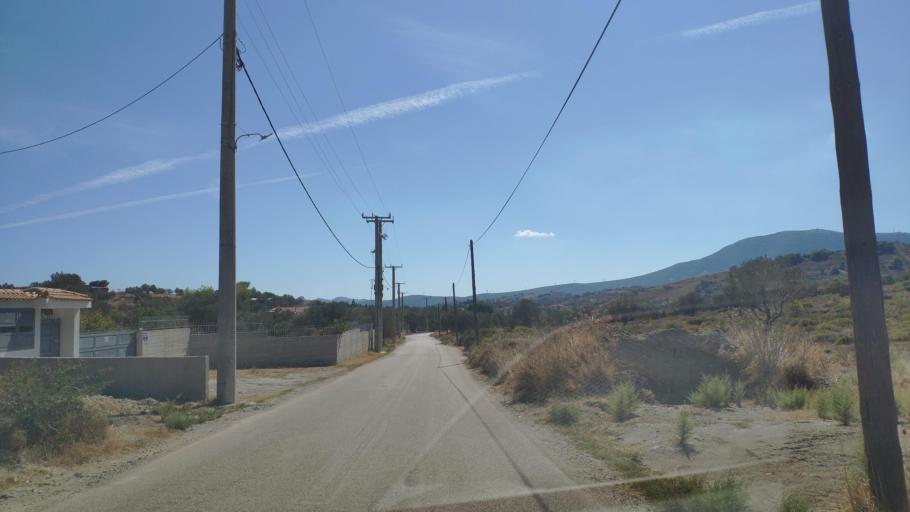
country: GR
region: Attica
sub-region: Nomarchia Anatolikis Attikis
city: Kouvaras
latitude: 37.8314
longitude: 23.9915
